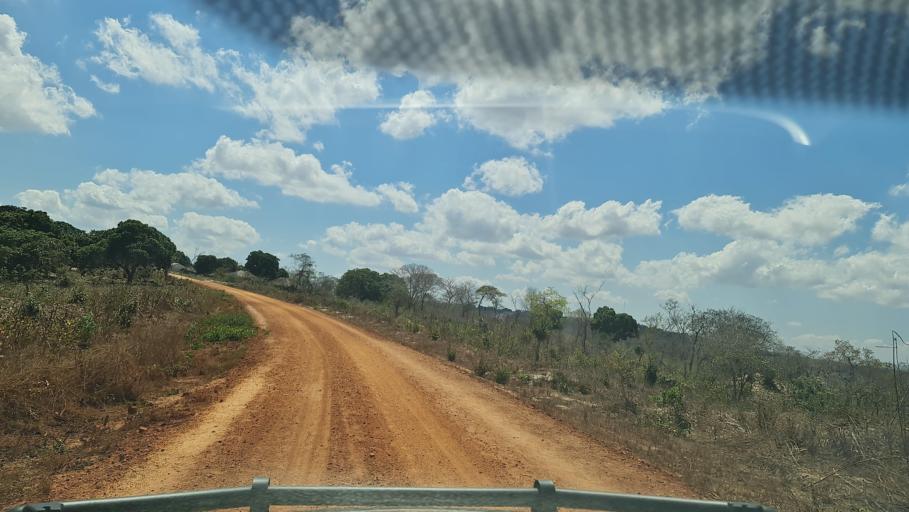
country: MZ
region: Nampula
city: Nacala
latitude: -14.1736
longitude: 40.2417
